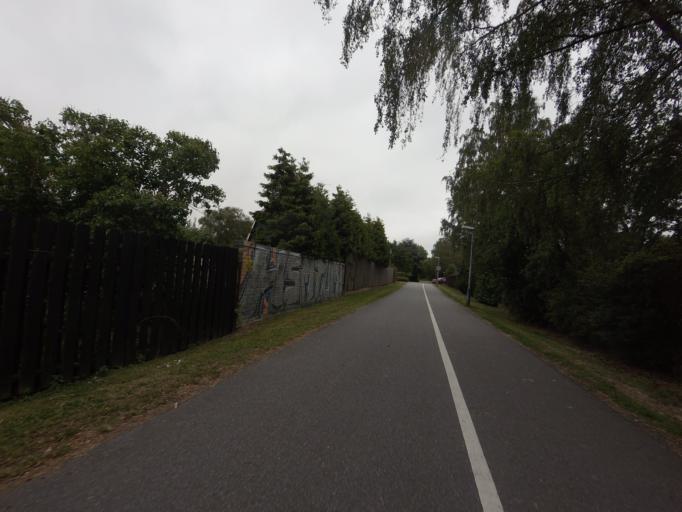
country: SE
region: Skane
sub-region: Malmo
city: Malmoe
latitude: 55.5696
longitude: 12.9932
